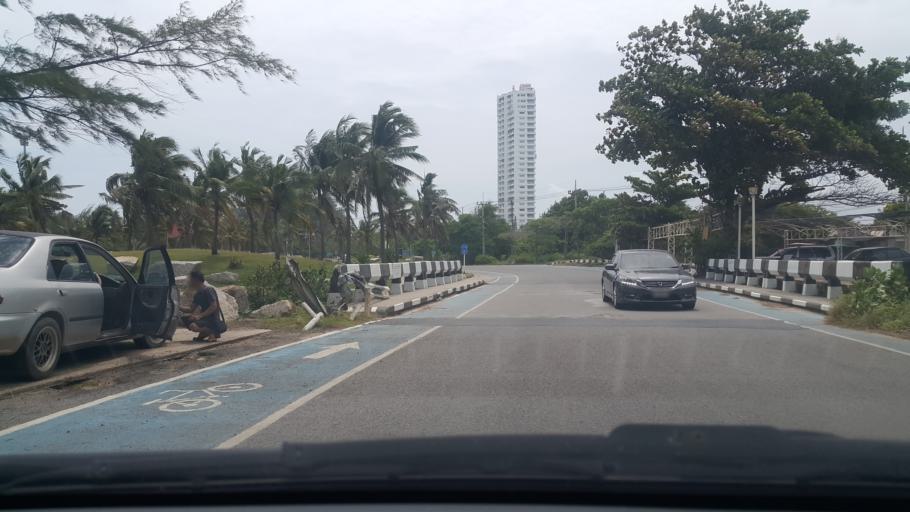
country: TH
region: Rayong
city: Rayong
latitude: 12.6104
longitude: 101.3861
